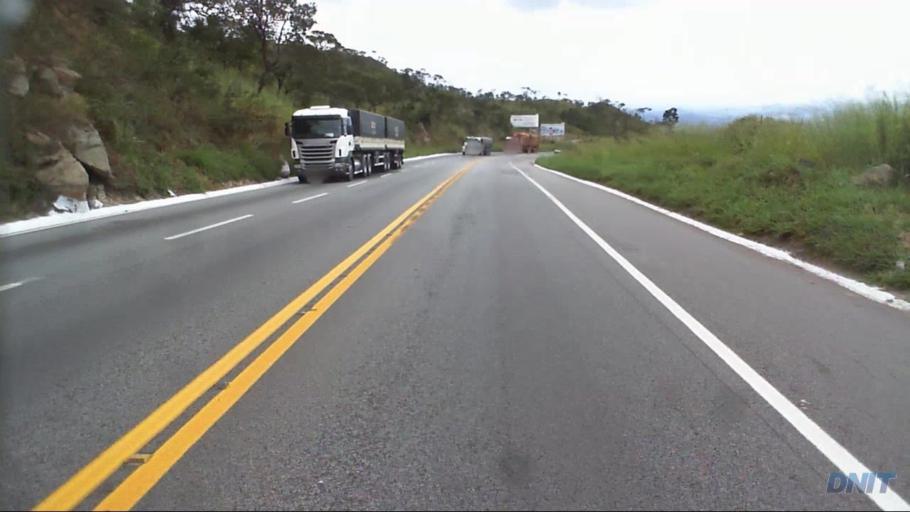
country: BR
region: Minas Gerais
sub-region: Caete
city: Caete
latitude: -19.7883
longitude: -43.7082
